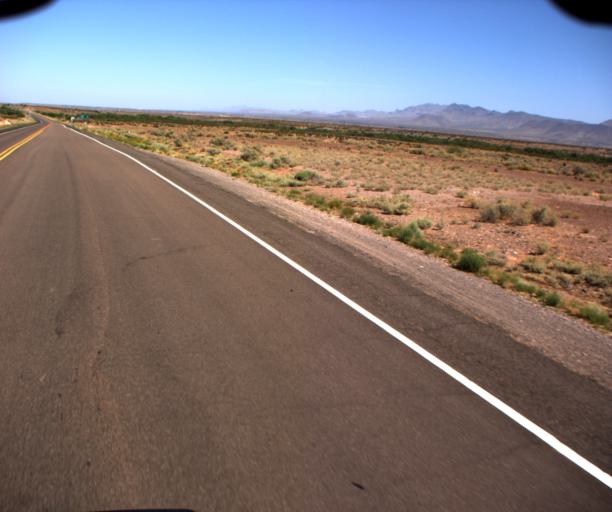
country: US
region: Arizona
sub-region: Graham County
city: Safford
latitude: 32.7944
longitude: -109.5549
